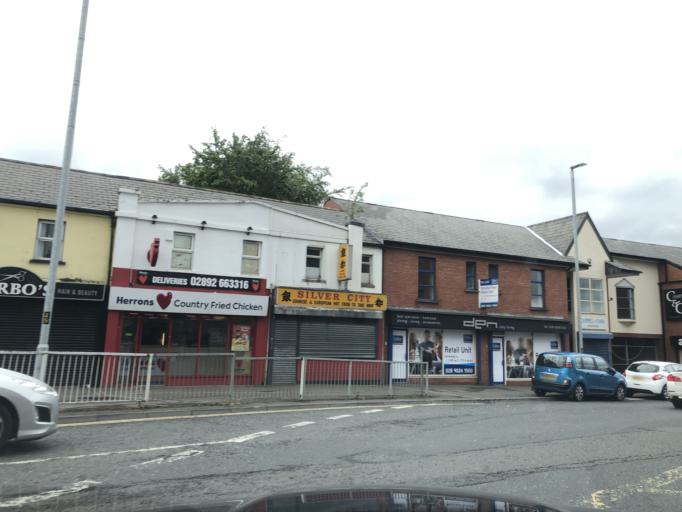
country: GB
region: Northern Ireland
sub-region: Lisburn District
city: Lisburn
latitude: 54.5099
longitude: -6.0536
